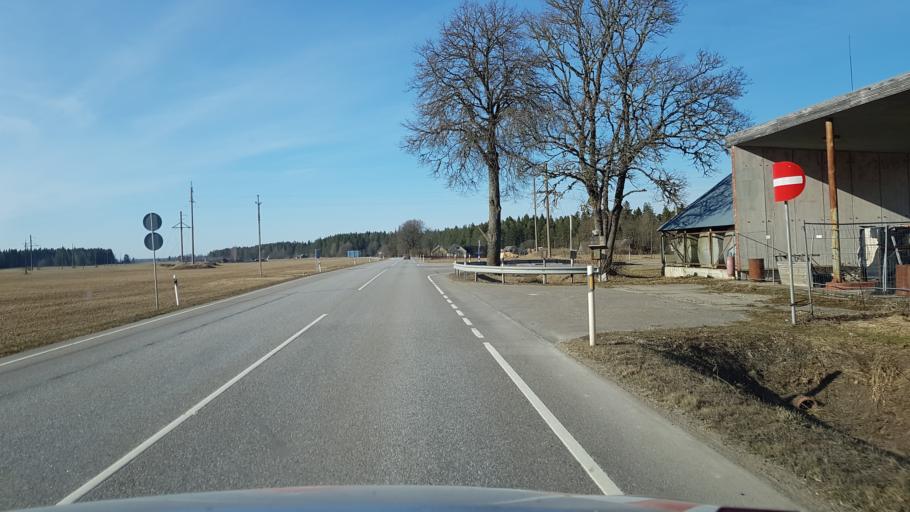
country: EE
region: Laeaene-Virumaa
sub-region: Vinni vald
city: Vinni
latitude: 59.1797
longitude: 26.5774
